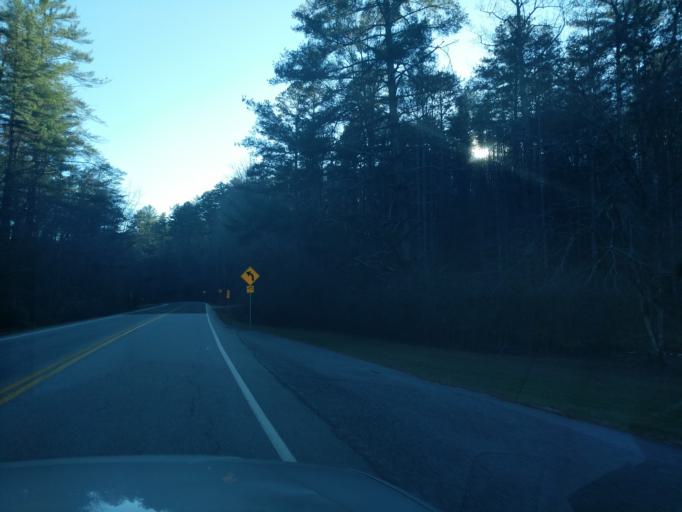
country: US
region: Georgia
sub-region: Rabun County
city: Clayton
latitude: 34.8171
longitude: -83.3190
